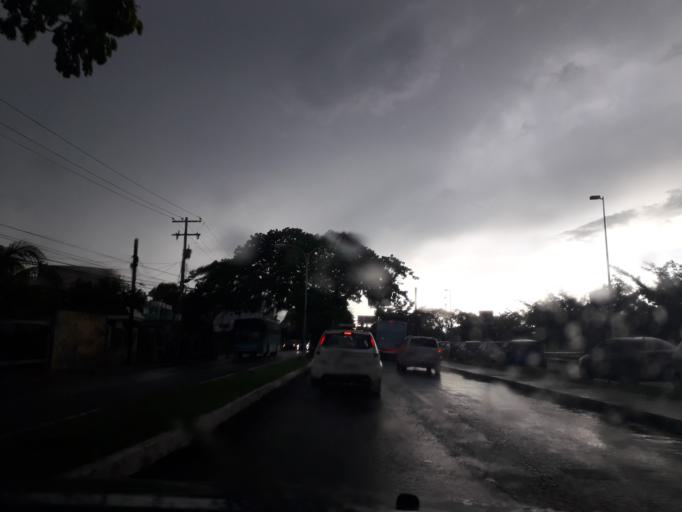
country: MX
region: Yucatan
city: Merida
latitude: 20.9778
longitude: -89.6444
